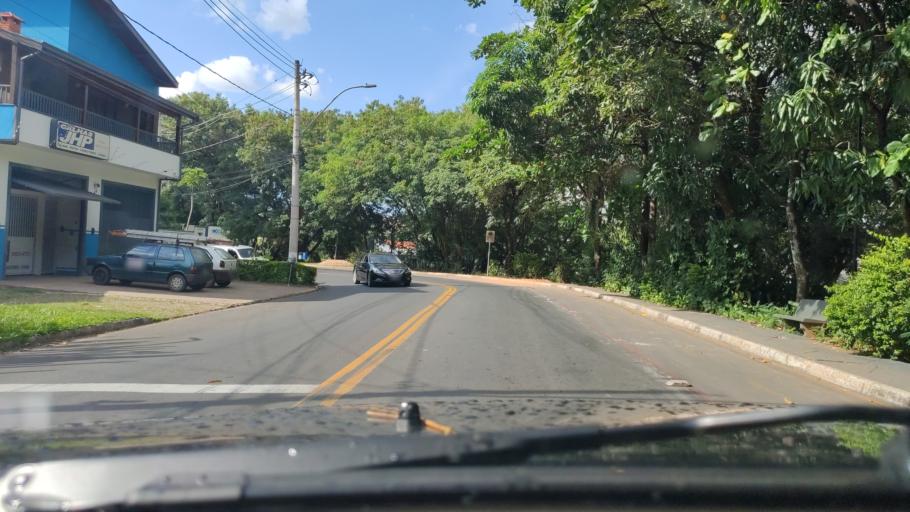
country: BR
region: Sao Paulo
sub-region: Itapira
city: Itapira
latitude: -22.4368
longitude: -46.8180
